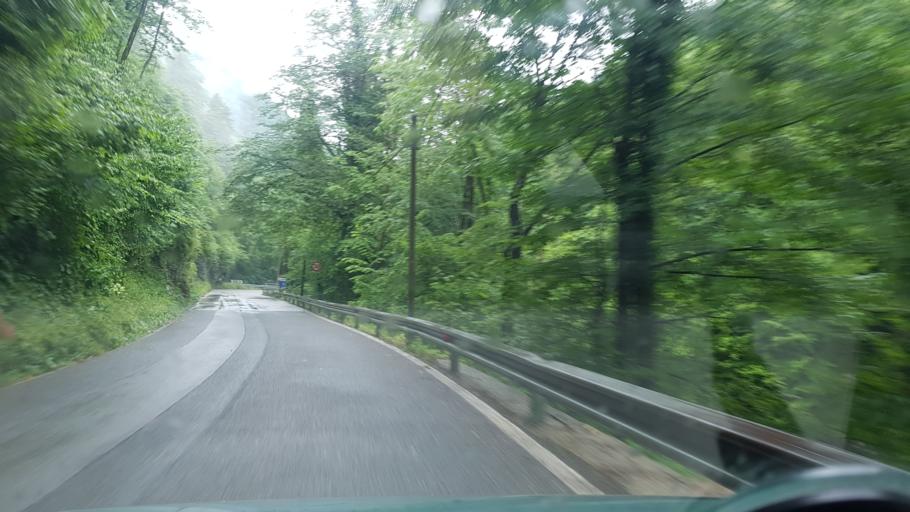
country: IT
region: Friuli Venezia Giulia
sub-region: Provincia di Udine
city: Taipana
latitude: 46.2482
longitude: 13.3114
